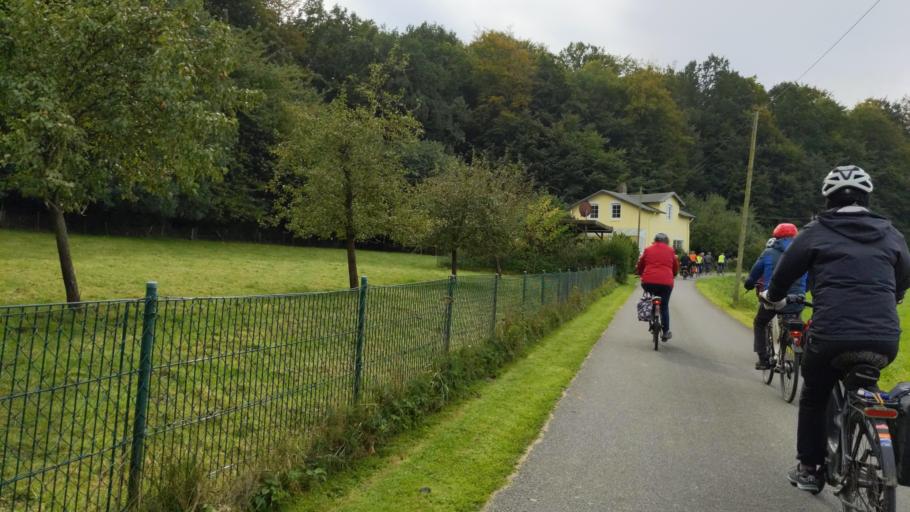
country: DE
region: Schleswig-Holstein
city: Rehhorst
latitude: 53.8649
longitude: 10.4771
